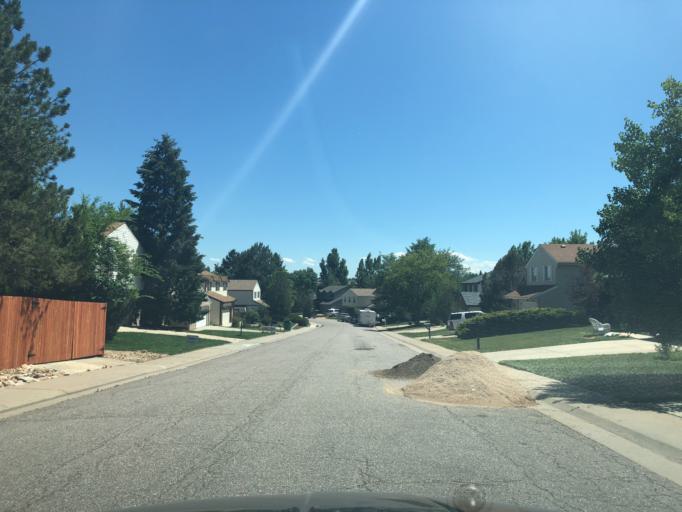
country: US
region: Colorado
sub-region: Arapahoe County
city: Dove Valley
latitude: 39.6176
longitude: -104.7872
